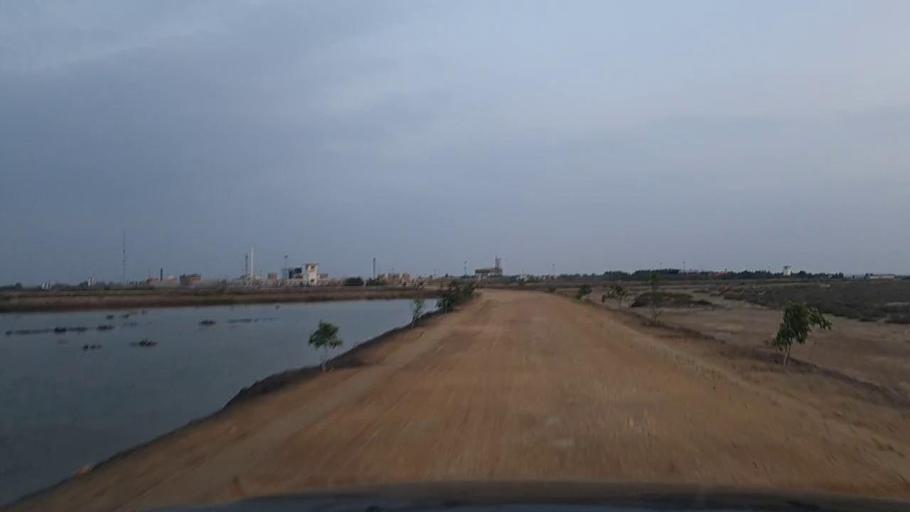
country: PK
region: Sindh
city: Jati
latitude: 24.4923
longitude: 68.3901
